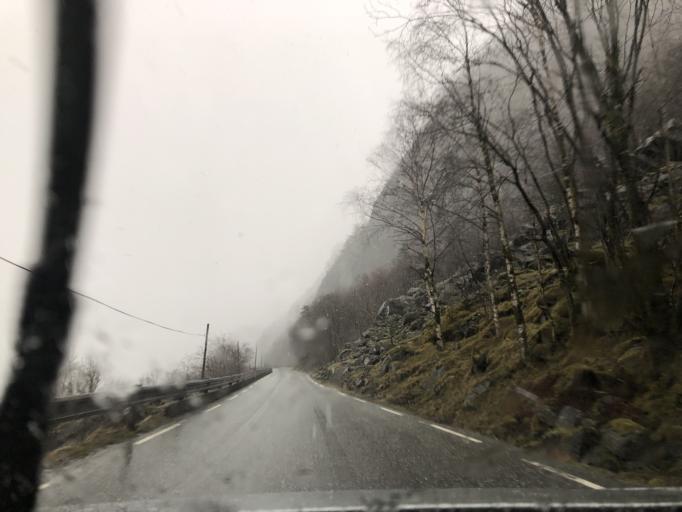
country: NO
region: Rogaland
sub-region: Suldal
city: Sand
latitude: 59.4099
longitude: 6.2139
